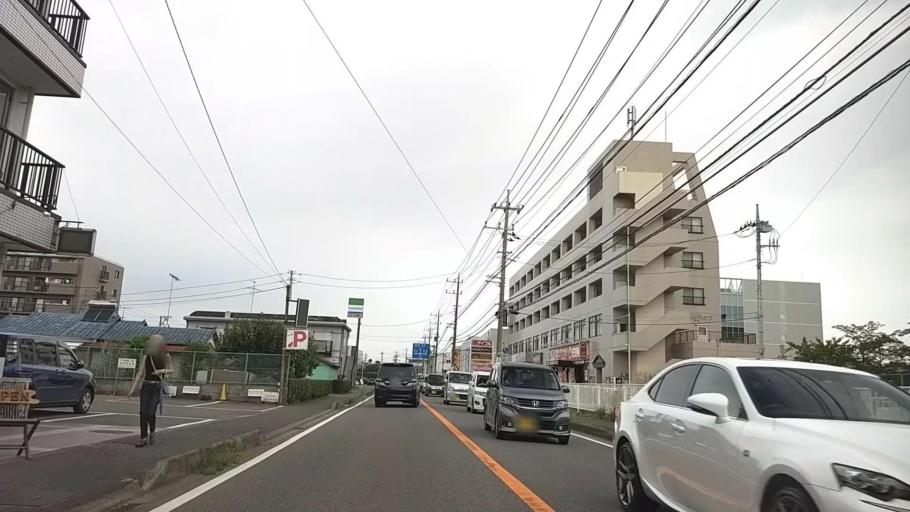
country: JP
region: Kanagawa
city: Zama
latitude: 35.4600
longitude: 139.3866
